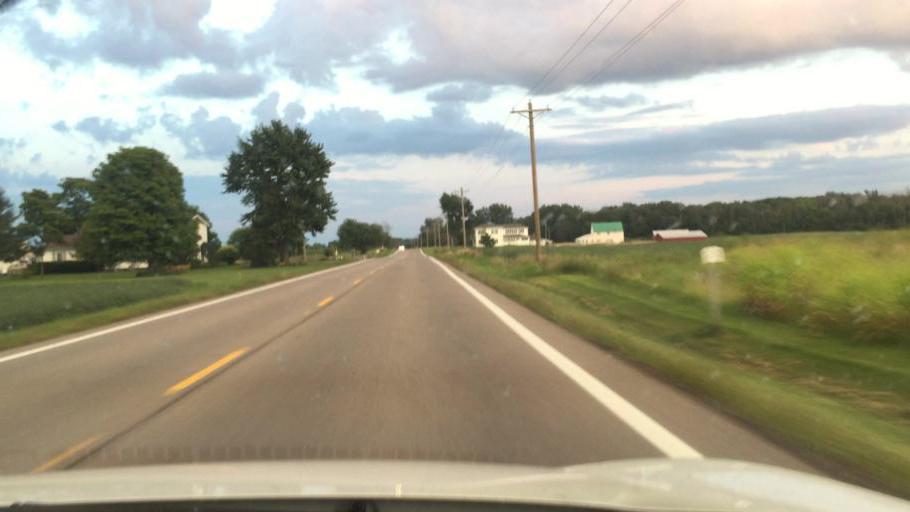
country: US
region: Ohio
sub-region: Champaign County
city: Mechanicsburg
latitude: 40.0543
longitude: -83.5292
